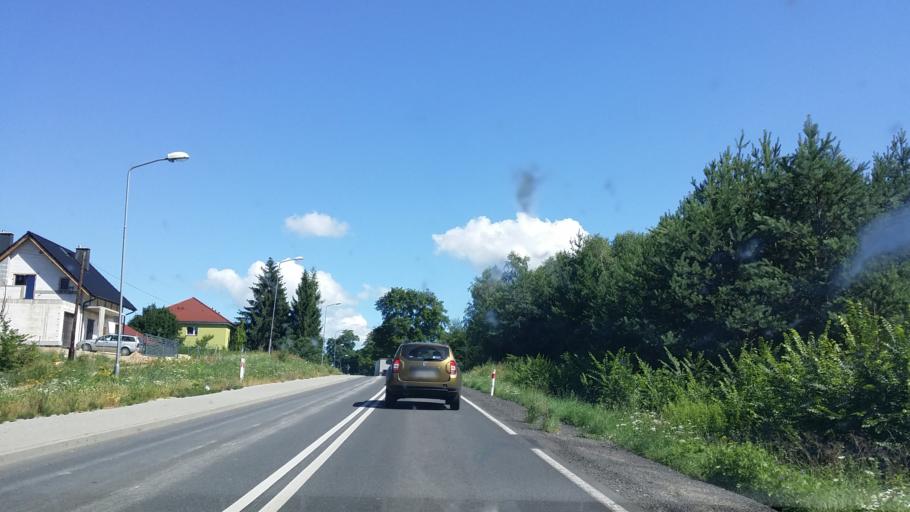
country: PL
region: West Pomeranian Voivodeship
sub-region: Powiat drawski
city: Kalisz Pomorski
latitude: 53.3060
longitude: 15.9090
